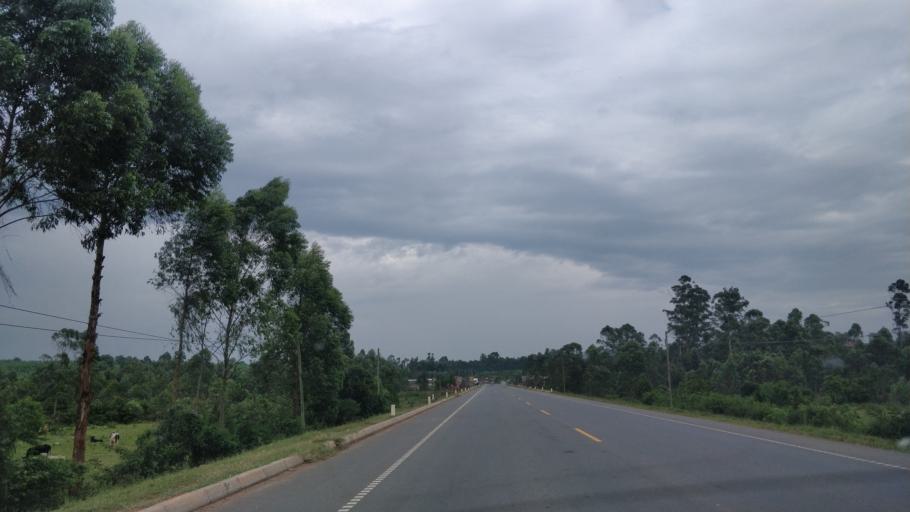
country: UG
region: Western Region
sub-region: Sheema District
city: Kibingo
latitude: -0.6689
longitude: 30.4407
